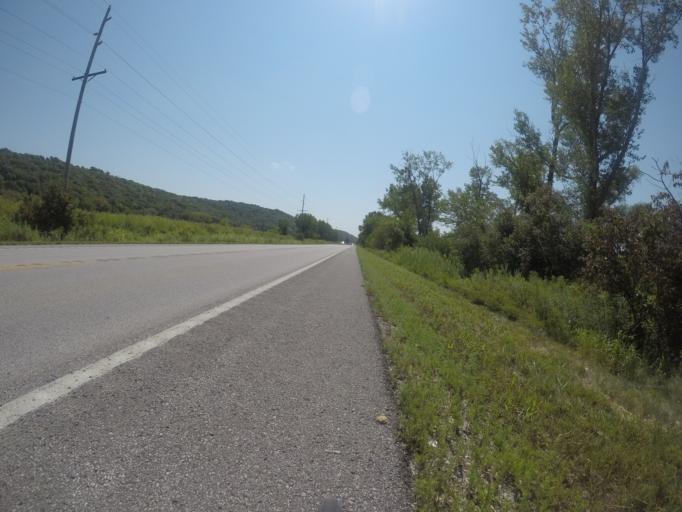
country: US
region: Kansas
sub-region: Atchison County
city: Atchison
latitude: 39.5038
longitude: -95.0094
